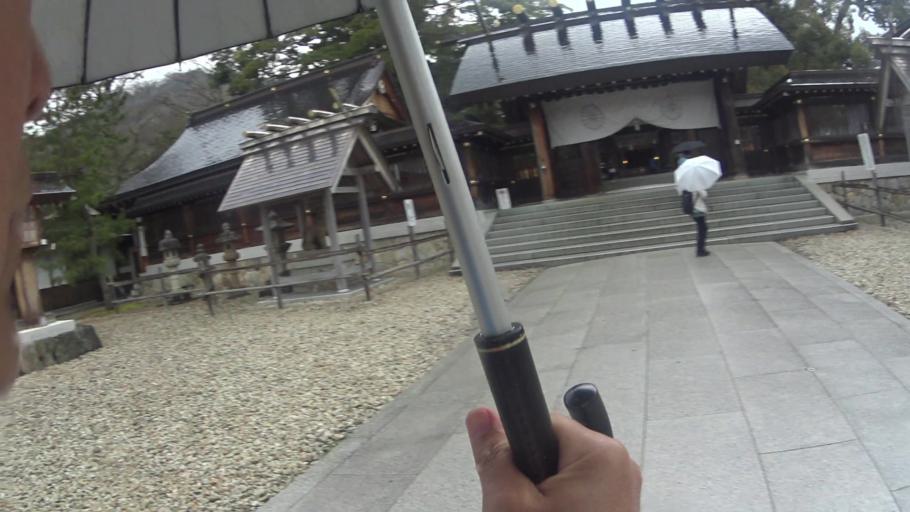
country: JP
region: Kyoto
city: Miyazu
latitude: 35.5824
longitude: 135.1966
